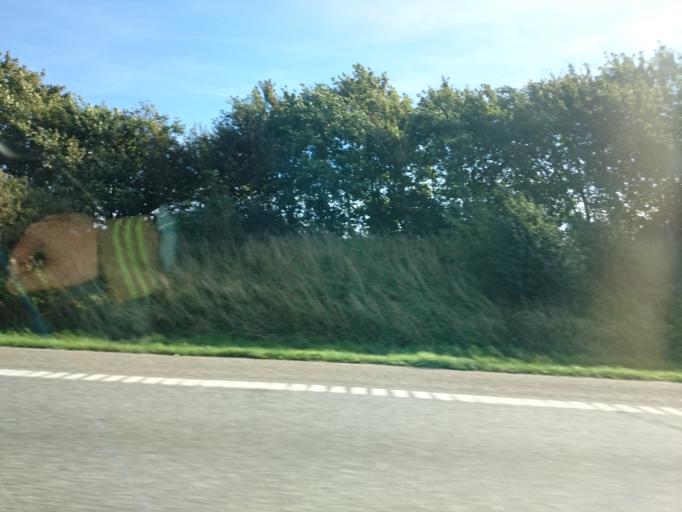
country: DK
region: Central Jutland
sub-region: Skanderborg Kommune
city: Stilling
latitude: 56.0782
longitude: 10.0058
